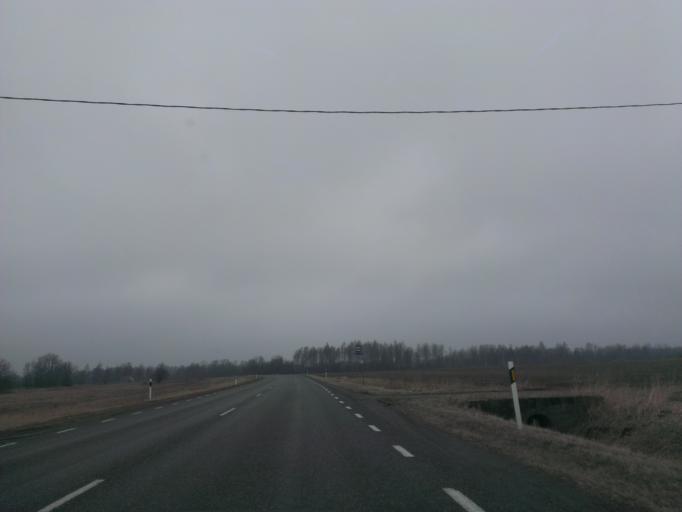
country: EE
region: Paernumaa
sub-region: Audru vald
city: Audru
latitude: 58.5014
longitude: 24.1204
